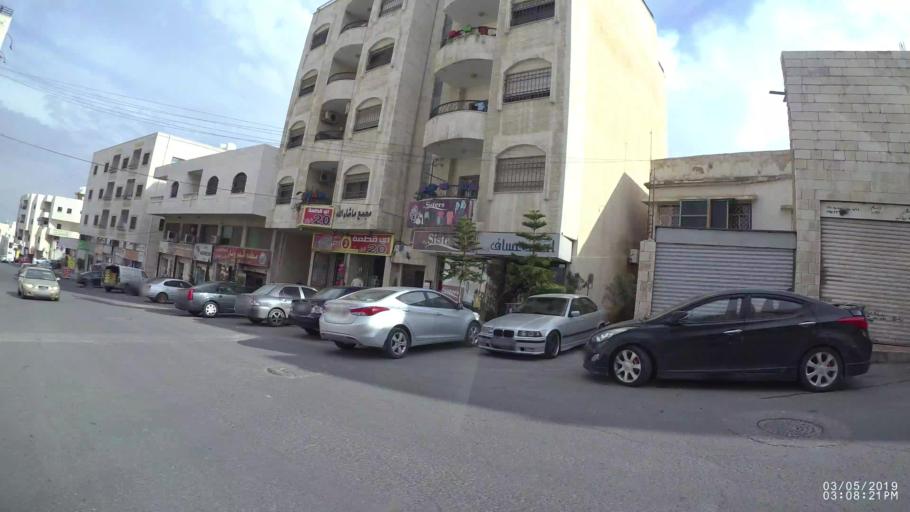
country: JO
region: Amman
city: Amman
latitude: 31.9990
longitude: 35.9485
